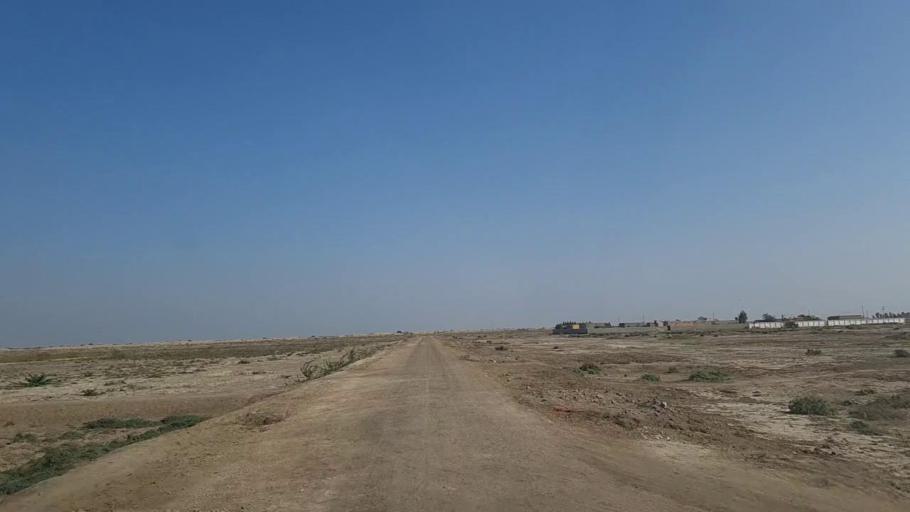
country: PK
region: Sindh
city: Digri
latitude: 25.0723
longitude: 69.2232
